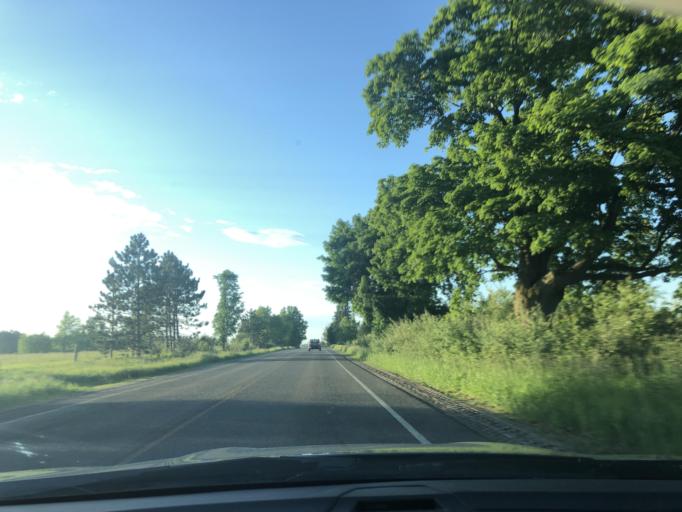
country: US
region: Michigan
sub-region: Missaukee County
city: Lake City
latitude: 44.4052
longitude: -85.0755
